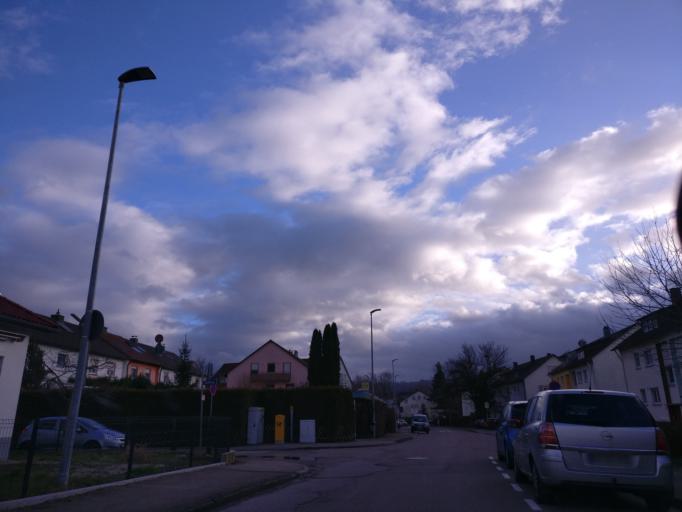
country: DE
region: Baden-Wuerttemberg
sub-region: Regierungsbezirk Stuttgart
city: Schorndorf
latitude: 48.8167
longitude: 9.5253
